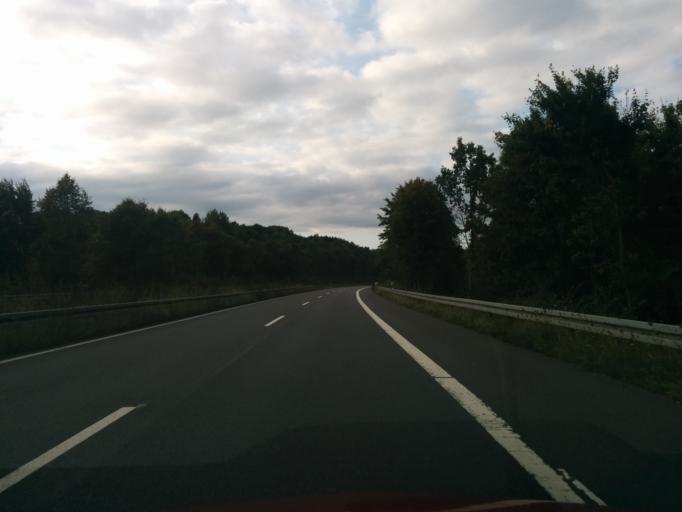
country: DE
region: Lower Saxony
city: Hoerden
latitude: 51.6921
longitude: 10.2940
